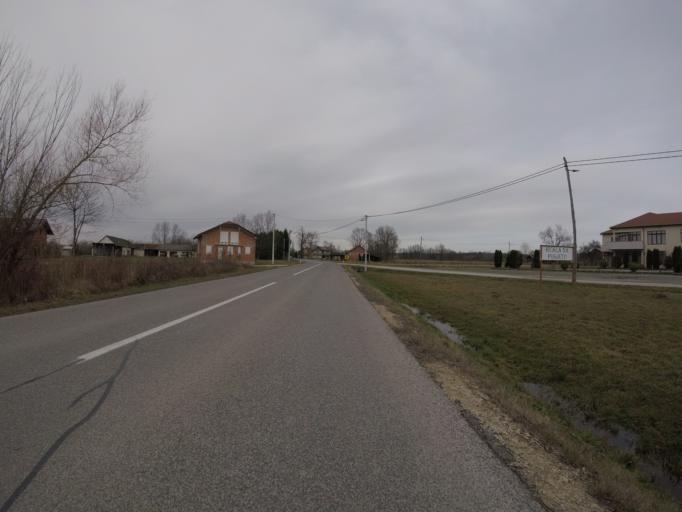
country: HR
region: Grad Zagreb
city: Horvati
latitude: 45.5673
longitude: 15.8638
